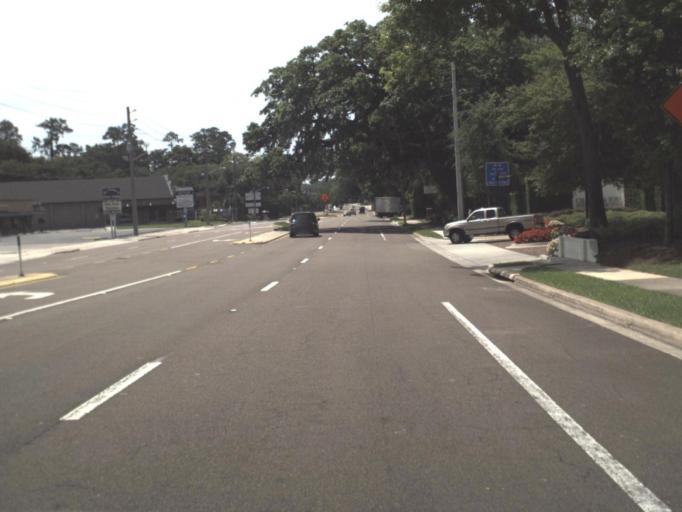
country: US
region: Florida
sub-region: Duval County
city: Jacksonville
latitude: 30.2668
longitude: -81.6481
